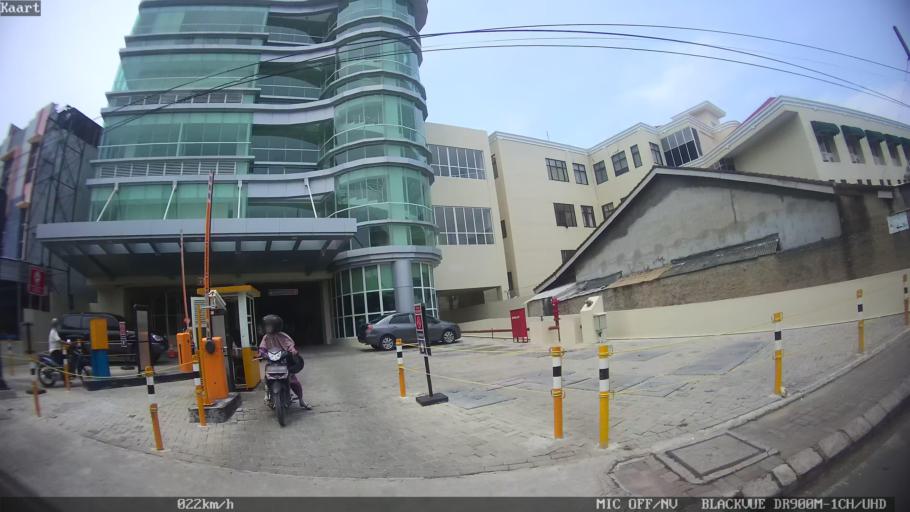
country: ID
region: Lampung
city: Bandarlampung
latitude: -5.4129
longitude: 105.2675
